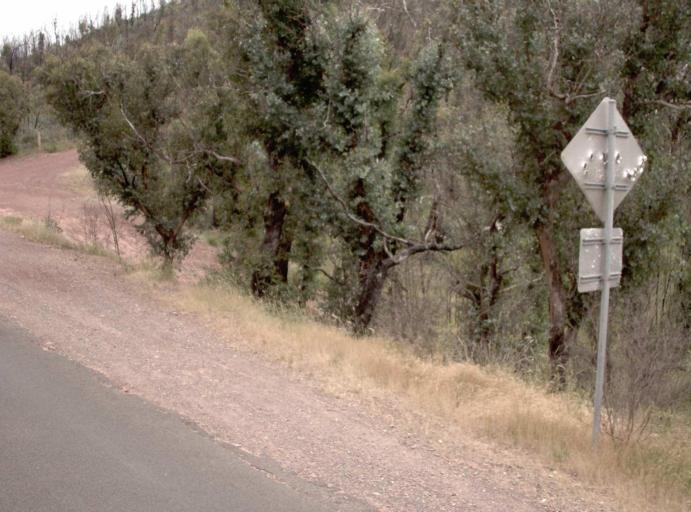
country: AU
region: Victoria
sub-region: Wellington
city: Heyfield
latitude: -37.7144
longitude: 146.6689
